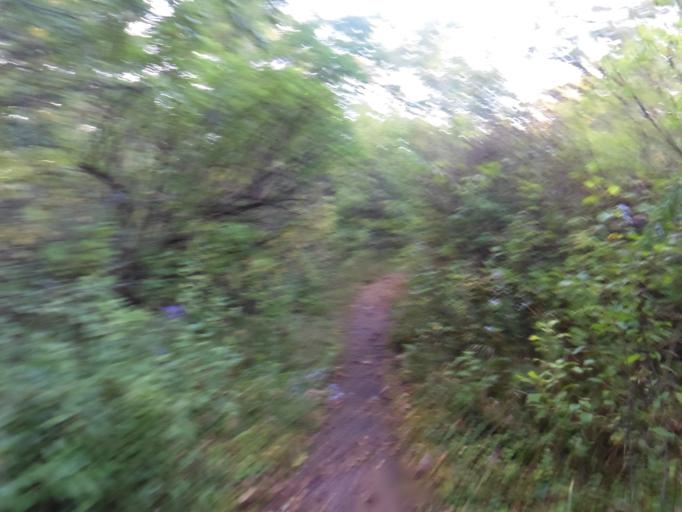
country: CA
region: Ontario
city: Bells Corners
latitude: 45.3712
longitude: -75.7927
